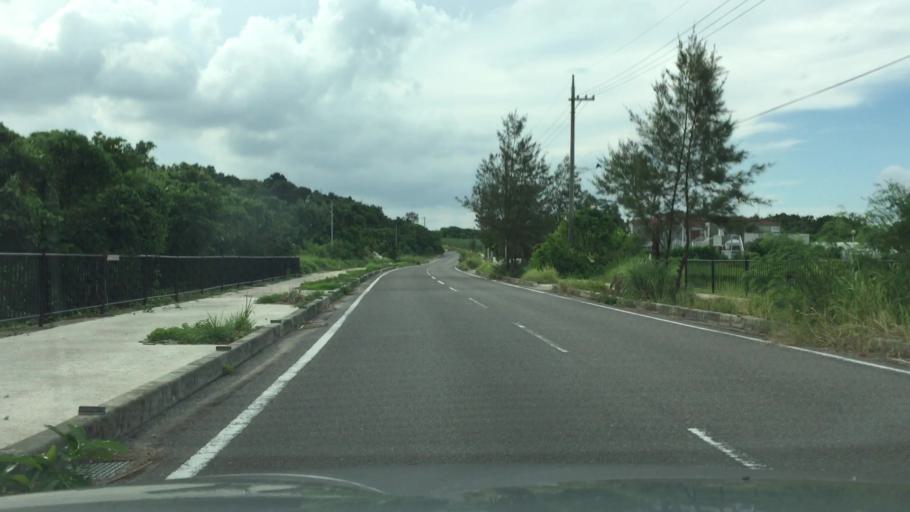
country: JP
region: Okinawa
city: Ishigaki
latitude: 24.4661
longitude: 124.1416
